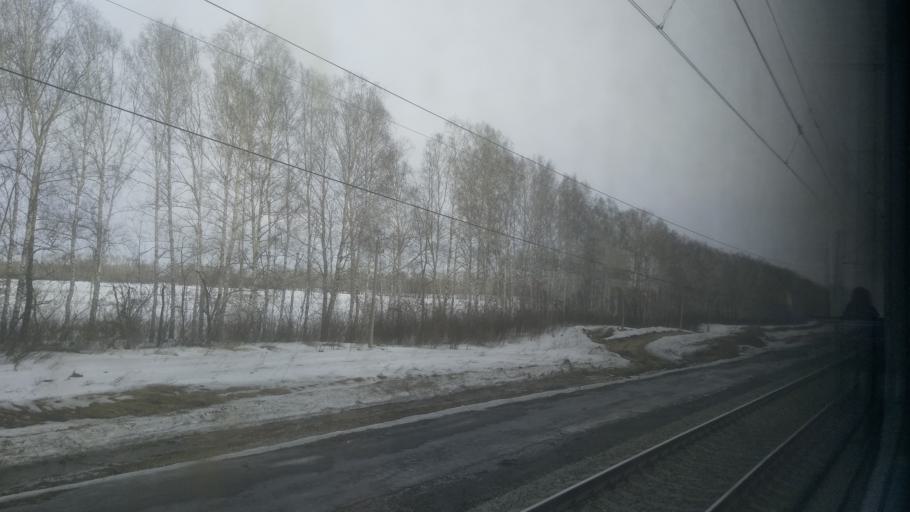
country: RU
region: Novosibirsk
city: Bolotnoye
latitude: 55.7069
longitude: 84.6019
